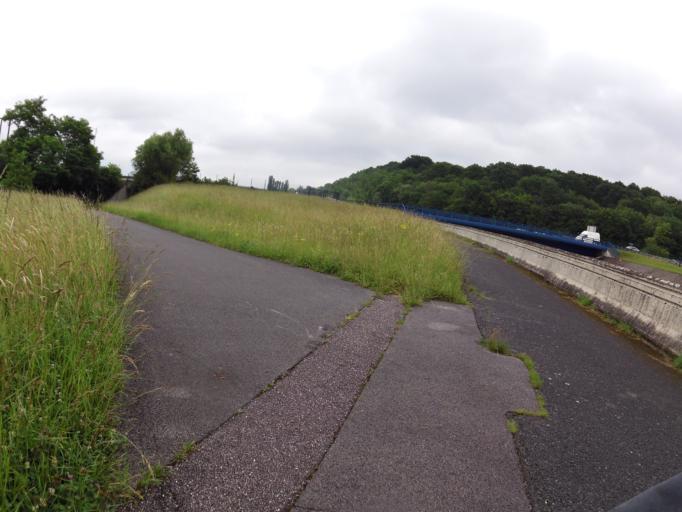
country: FR
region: Champagne-Ardenne
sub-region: Departement de la Haute-Marne
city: Saint-Dizier
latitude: 48.6160
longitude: 4.9160
